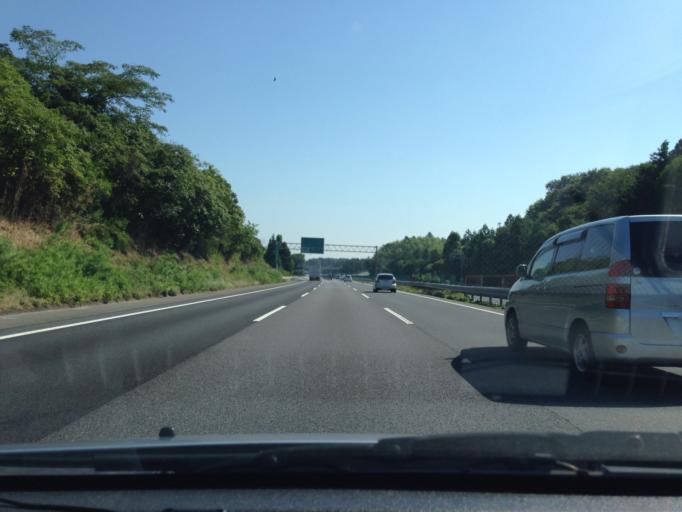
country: JP
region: Ibaraki
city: Ishioka
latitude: 36.1695
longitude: 140.2407
